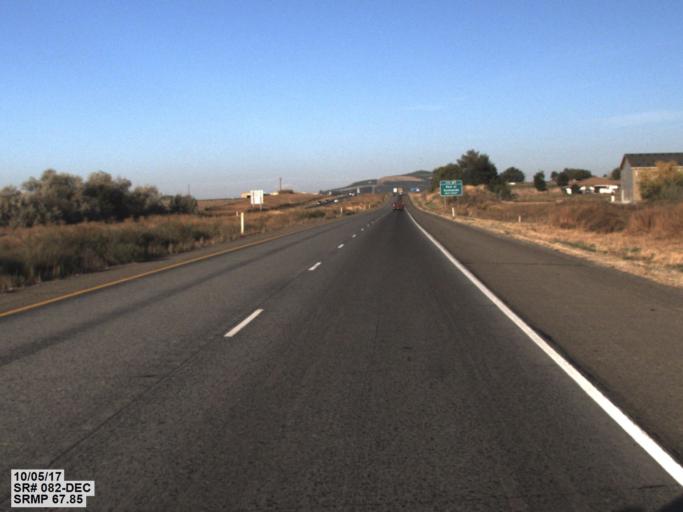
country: US
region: Washington
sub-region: Yakima County
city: Sunnyside
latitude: 46.3061
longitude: -120.0012
